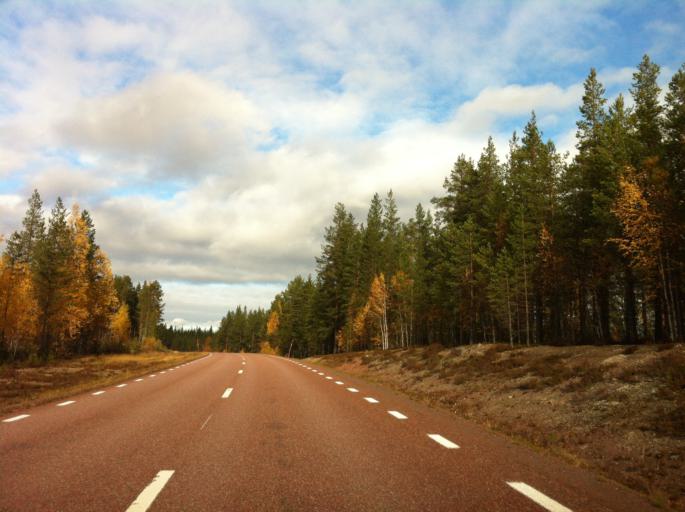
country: SE
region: Dalarna
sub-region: Alvdalens Kommun
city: AElvdalen
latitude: 61.5144
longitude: 13.3697
